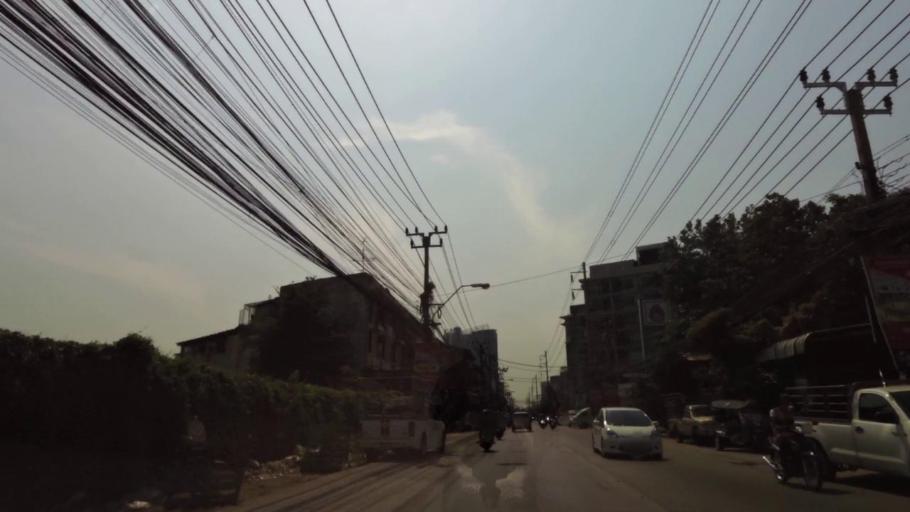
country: TH
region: Bangkok
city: Phra Khanong
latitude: 13.6539
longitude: 100.5931
